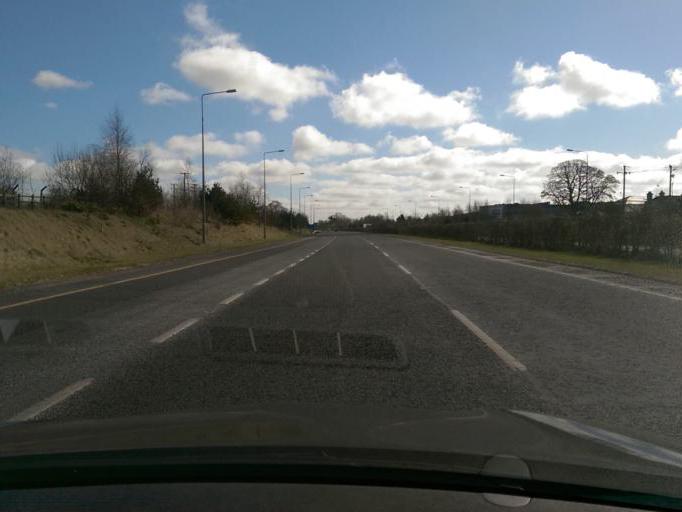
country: IE
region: Leinster
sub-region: An Mhi
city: Enfield
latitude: 53.4074
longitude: -6.8411
